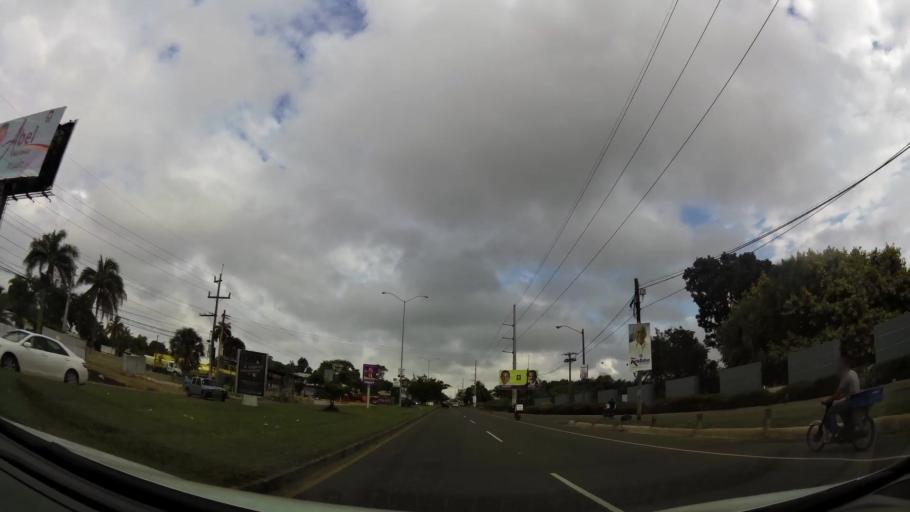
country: DO
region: Santiago
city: Licey al Medio
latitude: 19.4216
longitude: -70.6490
